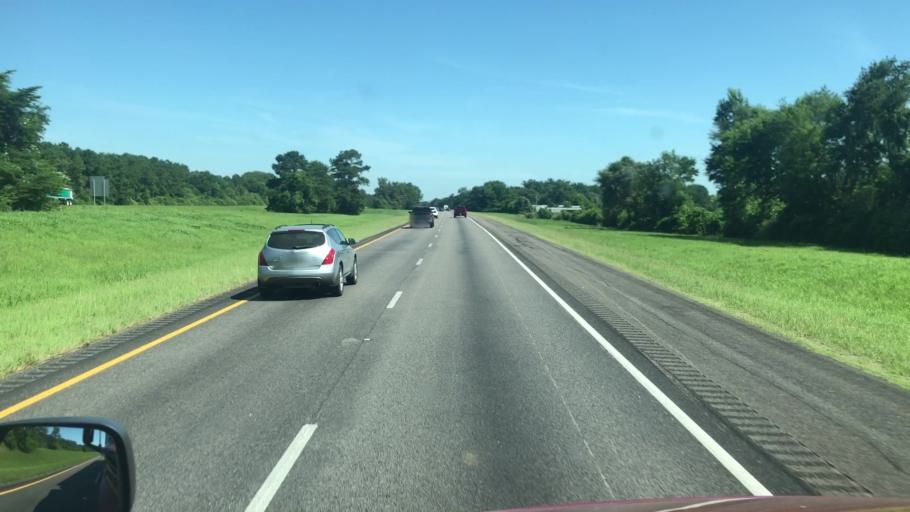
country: US
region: Alabama
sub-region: Autauga County
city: Pine Level
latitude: 32.5647
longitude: -86.4641
